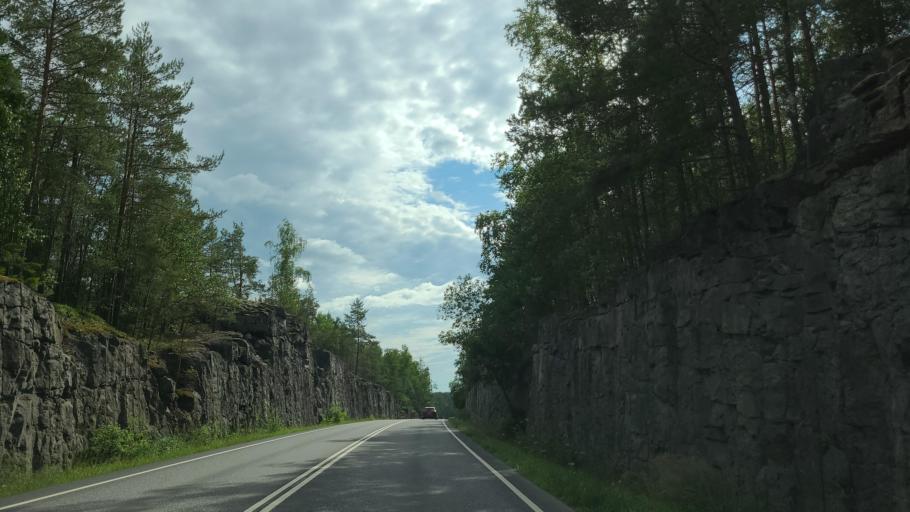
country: FI
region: Varsinais-Suomi
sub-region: Turku
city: Merimasku
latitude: 60.4553
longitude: 21.9086
